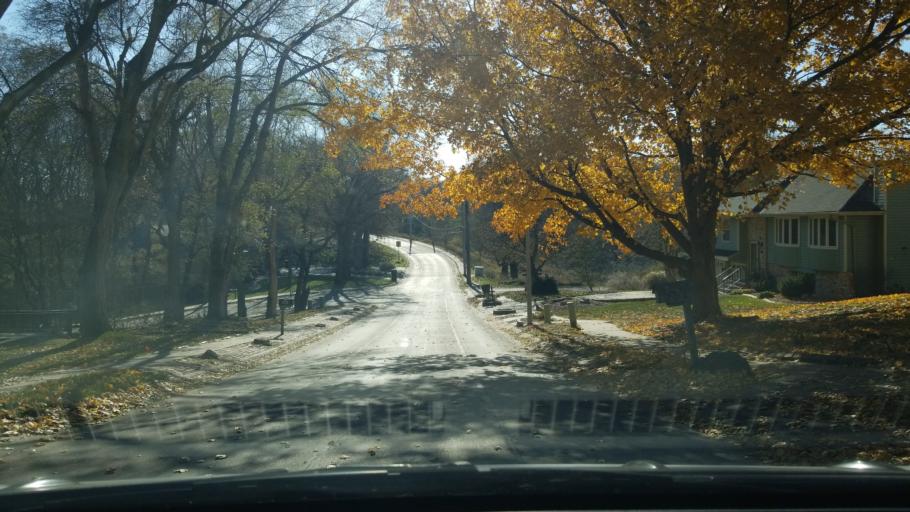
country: US
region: Nebraska
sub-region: Sarpy County
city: Bellevue
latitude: 41.1626
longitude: -95.9013
